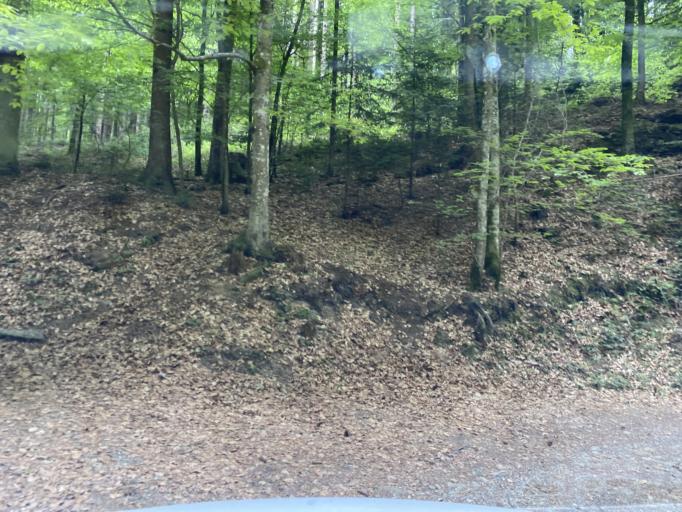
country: AT
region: Styria
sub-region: Politischer Bezirk Weiz
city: Baierdorf-Umgebung
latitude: 47.2984
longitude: 15.7070
